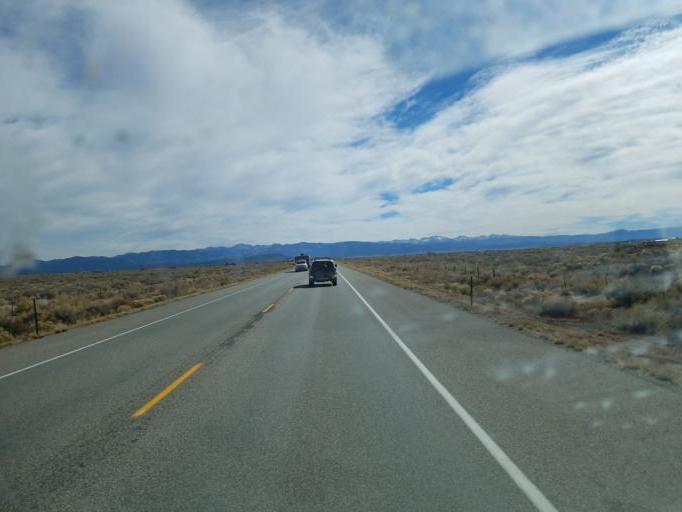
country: US
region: Colorado
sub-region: Costilla County
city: San Luis
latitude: 37.4490
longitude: -105.5408
